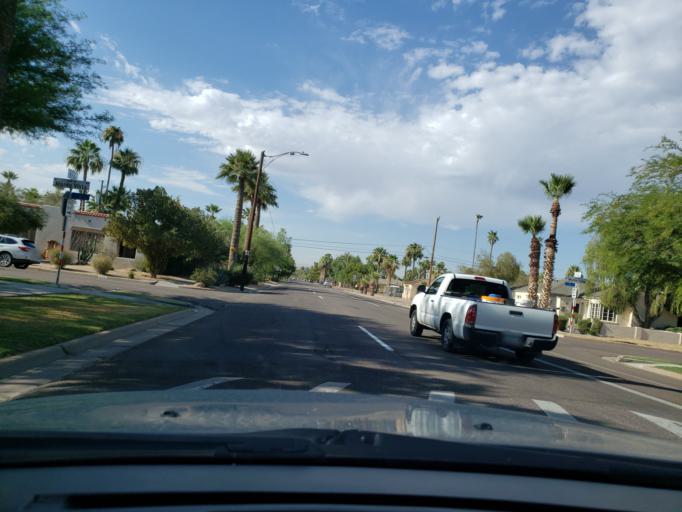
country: US
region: Arizona
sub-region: Maricopa County
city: Phoenix
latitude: 33.4714
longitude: -112.0802
